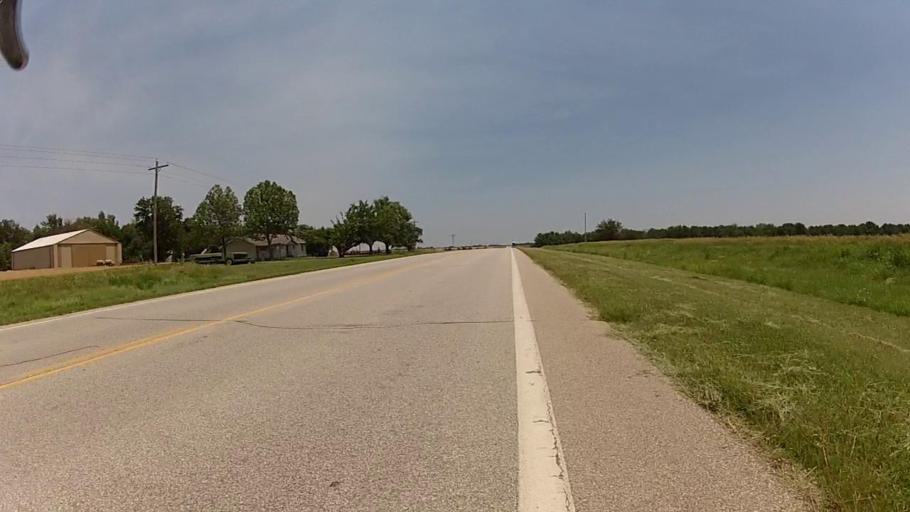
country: US
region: Kansas
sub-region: Cowley County
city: Arkansas City
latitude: 37.0569
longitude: -97.2321
